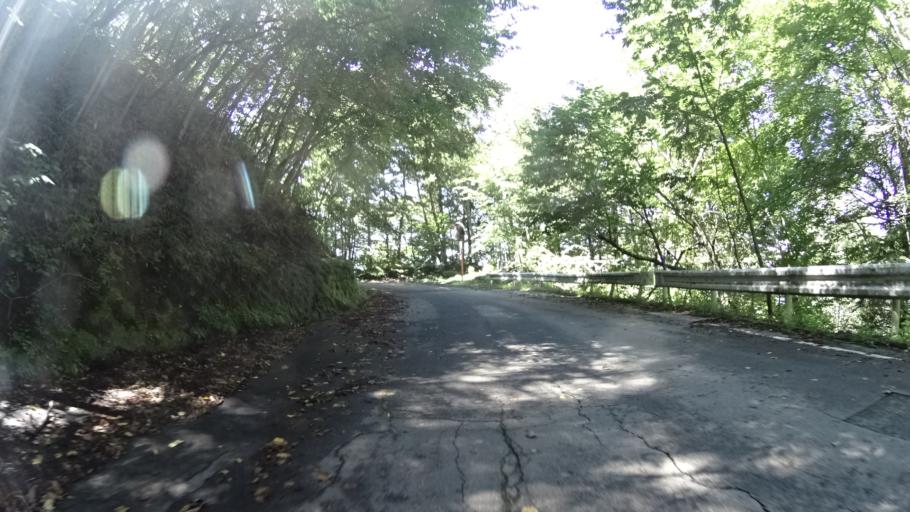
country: JP
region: Yamanashi
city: Enzan
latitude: 35.7355
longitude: 138.8321
